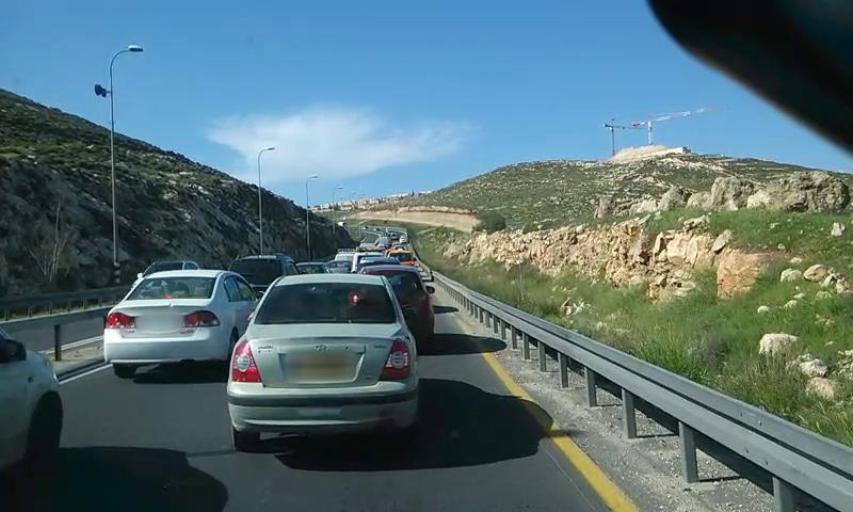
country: PS
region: West Bank
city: Hizma
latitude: 31.8358
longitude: 35.2543
